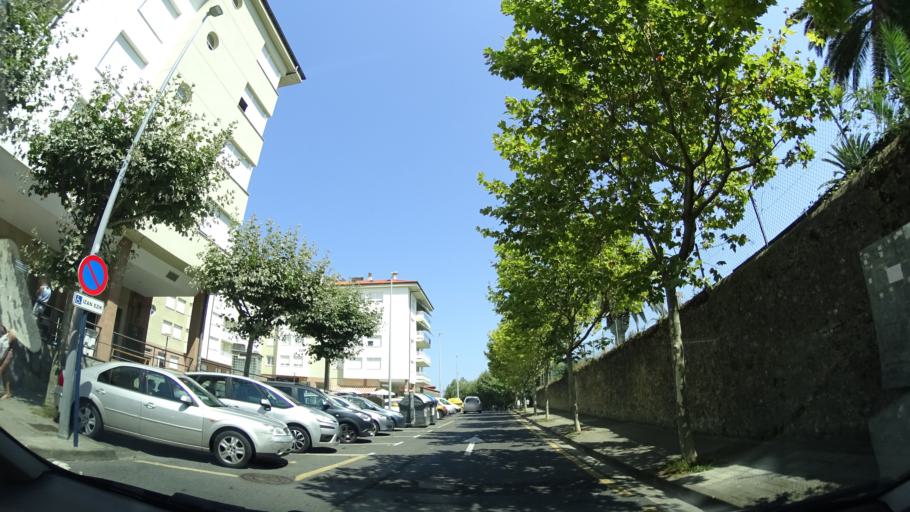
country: ES
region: Basque Country
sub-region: Bizkaia
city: Bermeo
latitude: 43.4226
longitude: -2.7228
